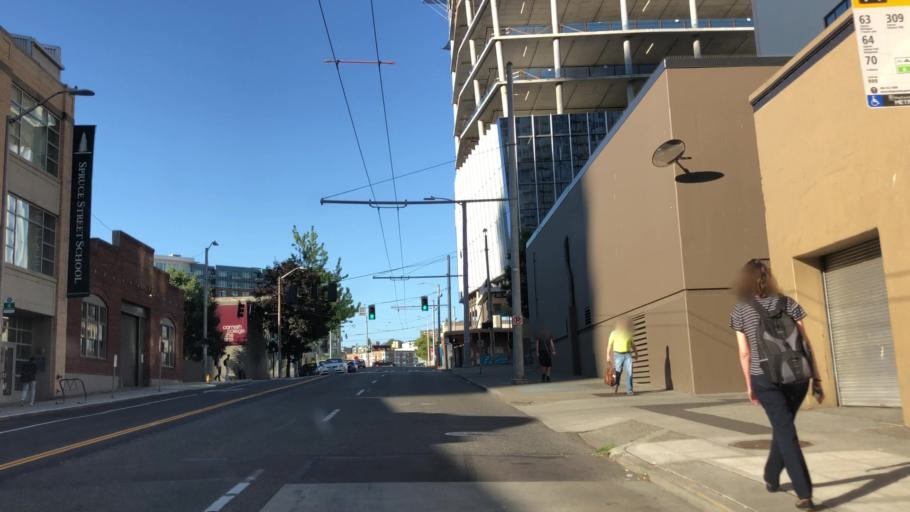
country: US
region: Washington
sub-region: King County
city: Seattle
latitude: 47.6166
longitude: -122.3355
